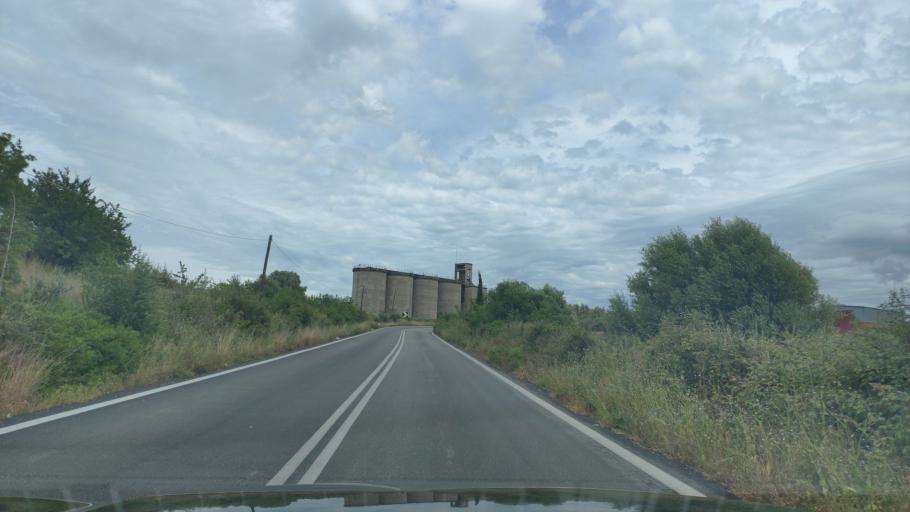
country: GR
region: West Greece
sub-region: Nomos Aitolias kai Akarnanias
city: Vonitsa
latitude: 38.8739
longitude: 20.8934
